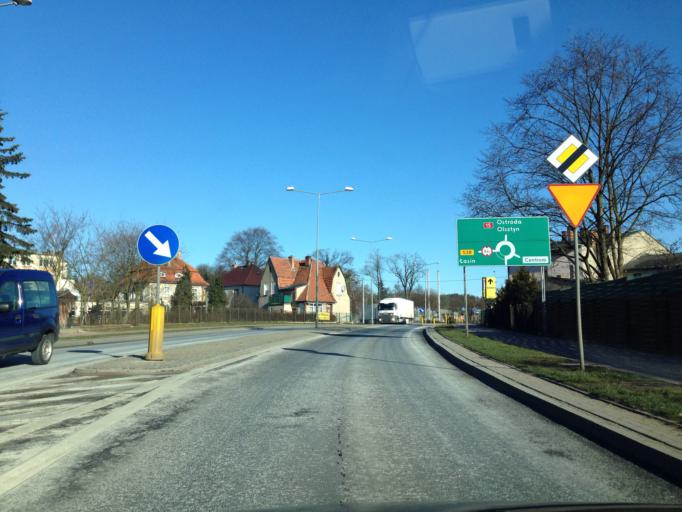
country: PL
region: Warmian-Masurian Voivodeship
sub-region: Powiat nowomiejski
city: Nowe Miasto Lubawskie
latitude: 53.4245
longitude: 19.5886
